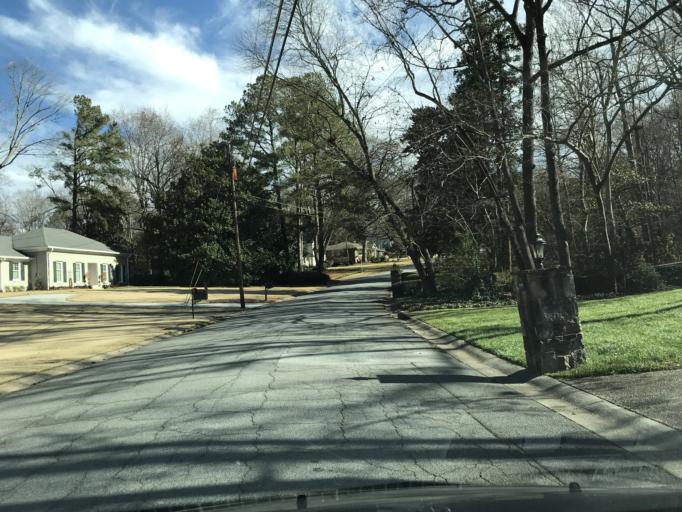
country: US
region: Georgia
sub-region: DeKalb County
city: North Atlanta
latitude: 33.8865
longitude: -84.3527
